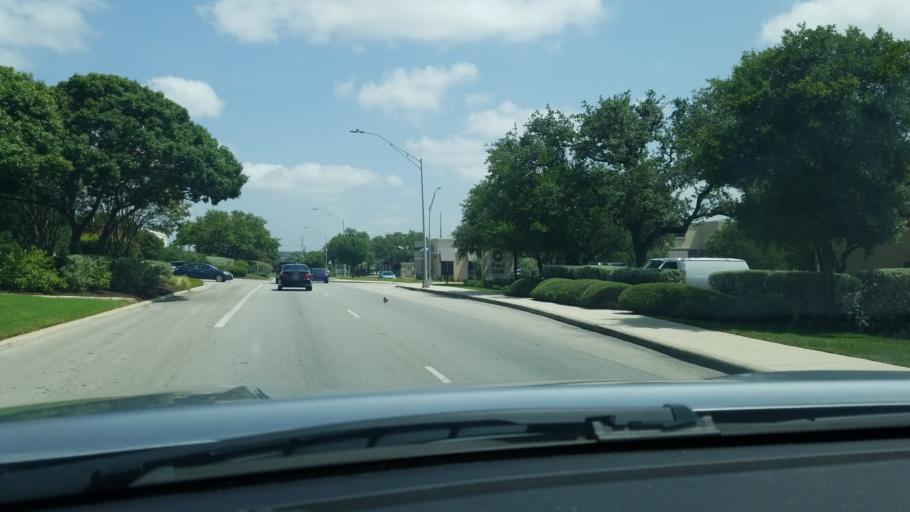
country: US
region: Texas
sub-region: Bexar County
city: Hollywood Park
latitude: 29.6113
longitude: -98.4931
